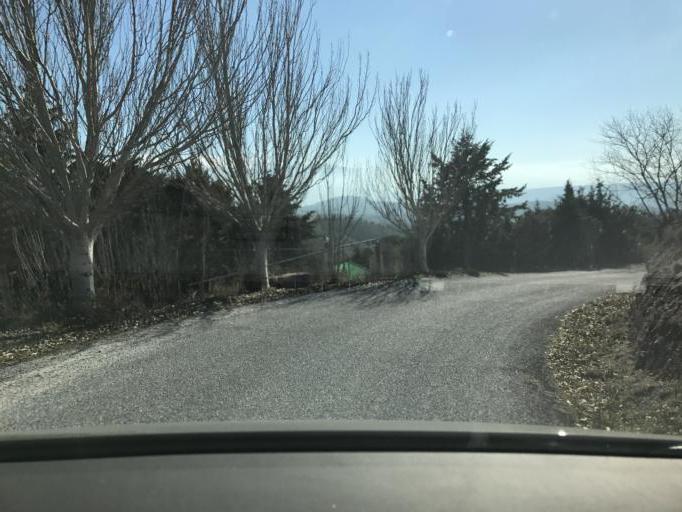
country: ES
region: Andalusia
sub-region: Provincia de Granada
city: Viznar
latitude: 37.2191
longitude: -3.5445
